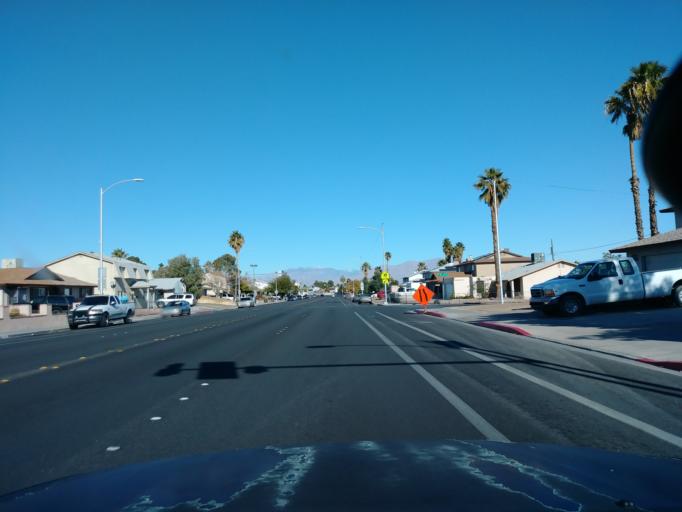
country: US
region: Nevada
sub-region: Clark County
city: Spring Valley
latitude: 36.1782
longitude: -115.2331
